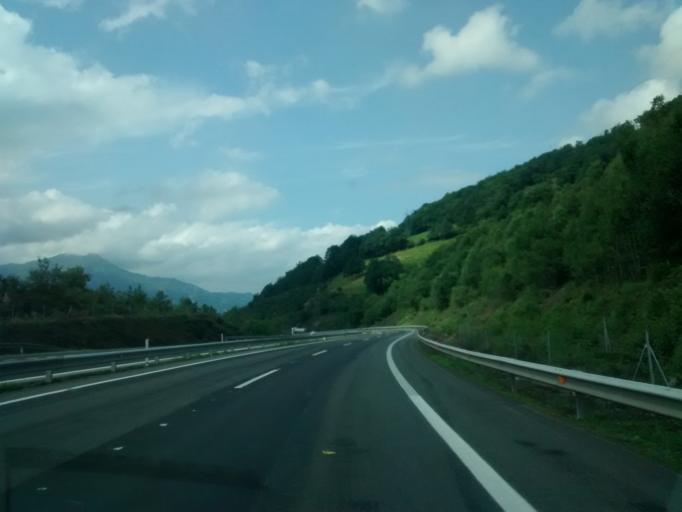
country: ES
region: Asturias
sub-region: Province of Asturias
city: Pola de Lena
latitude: 43.0435
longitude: -5.8195
